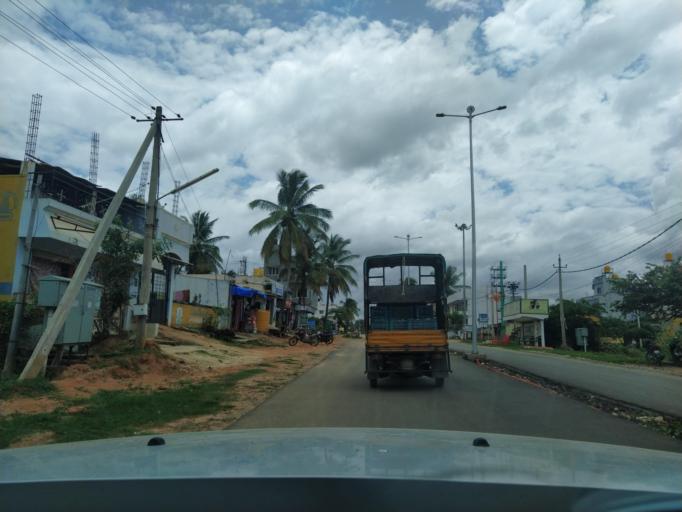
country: IN
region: Karnataka
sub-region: Tumkur
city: Tumkur
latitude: 13.3147
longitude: 77.1361
